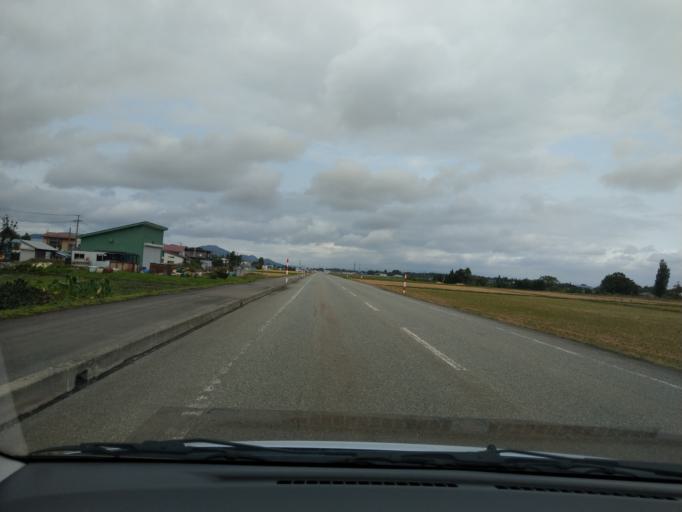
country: JP
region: Akita
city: Omagari
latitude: 39.3858
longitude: 140.4861
